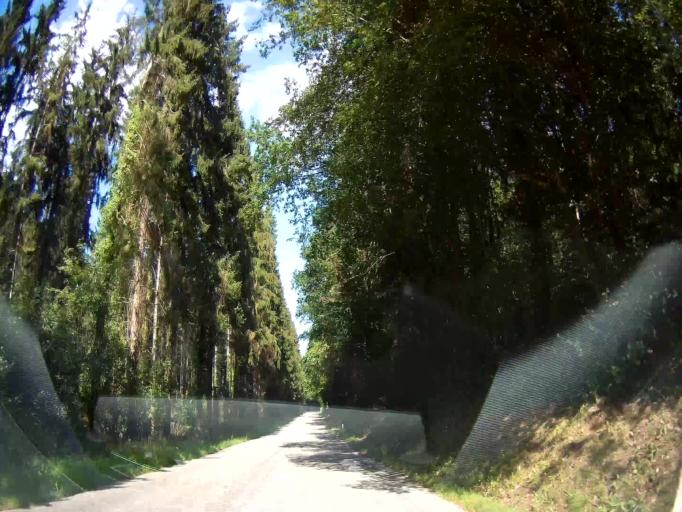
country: BE
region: Wallonia
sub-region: Province de Namur
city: Houyet
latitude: 50.2126
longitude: 4.9695
